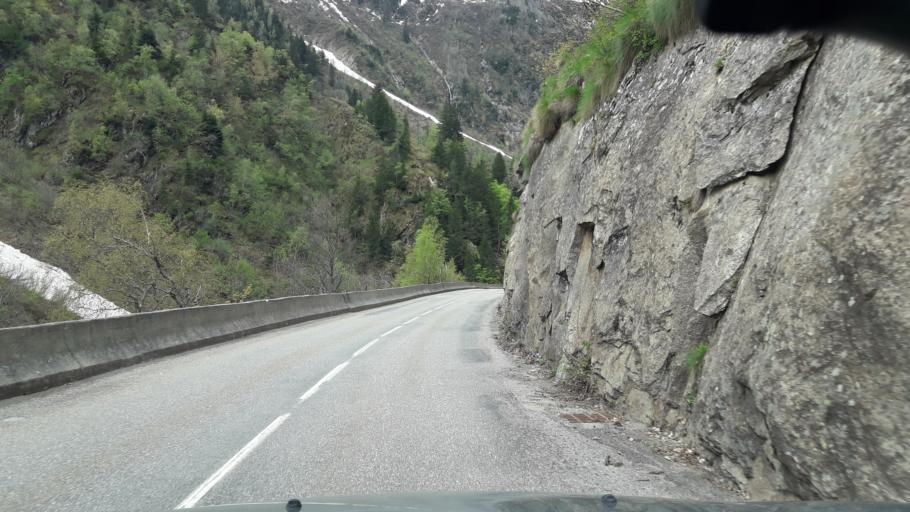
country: FR
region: Rhone-Alpes
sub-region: Departement de l'Isere
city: Huez
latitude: 45.2019
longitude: 6.0864
